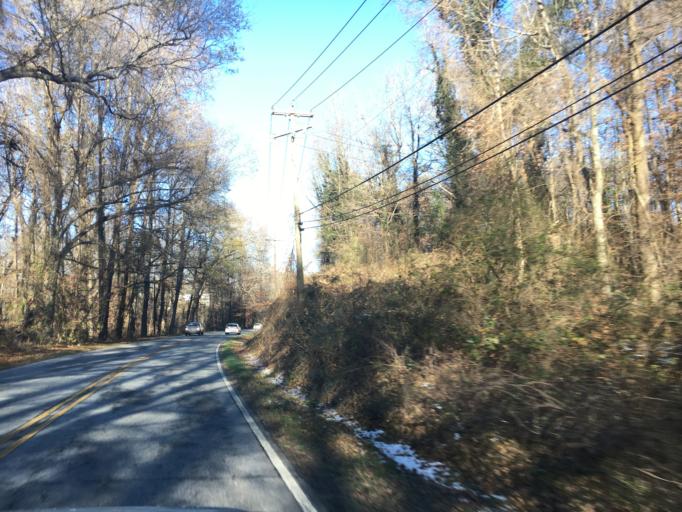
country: US
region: South Carolina
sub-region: Greenville County
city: Taylors
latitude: 34.9273
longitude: -82.2899
